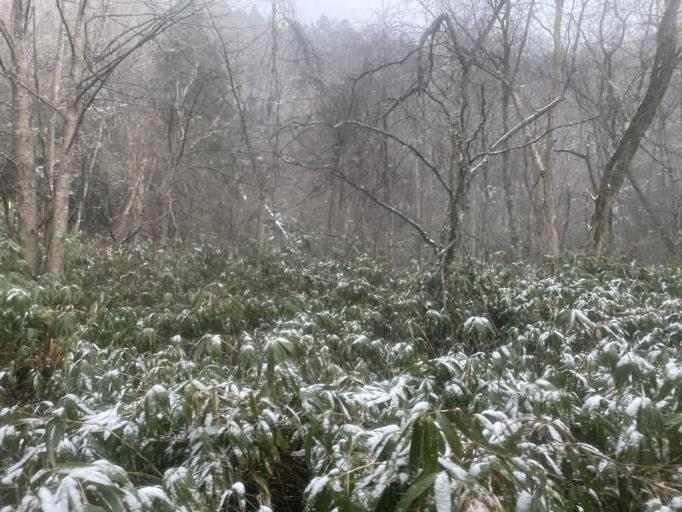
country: JP
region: Aomori
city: Goshogawara
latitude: 41.1017
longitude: 140.5281
